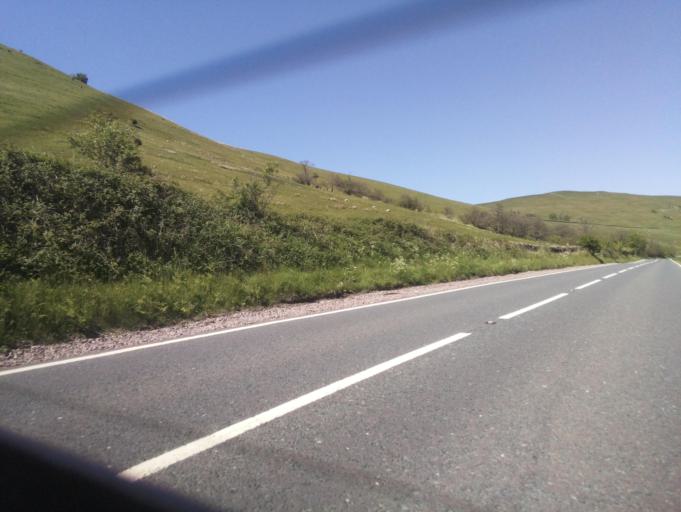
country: GB
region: Scotland
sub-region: Dumfries and Galloway
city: Langholm
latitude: 55.1781
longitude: -2.9946
